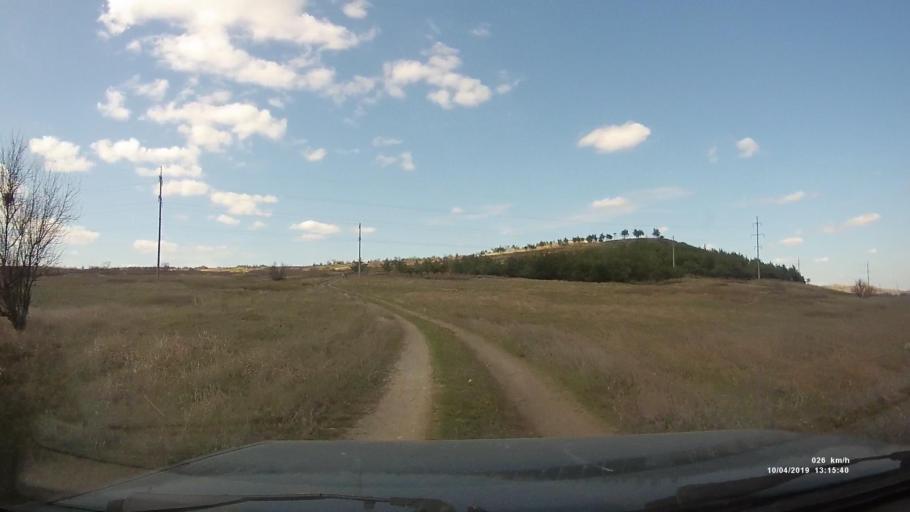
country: RU
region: Rostov
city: Masalovka
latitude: 48.4184
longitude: 40.2586
